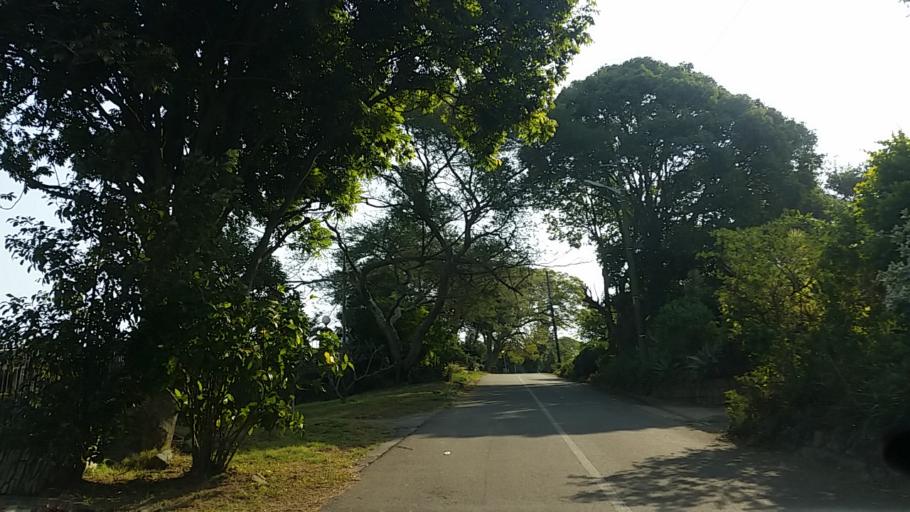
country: ZA
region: KwaZulu-Natal
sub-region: eThekwini Metropolitan Municipality
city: Berea
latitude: -29.8362
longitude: 30.9394
